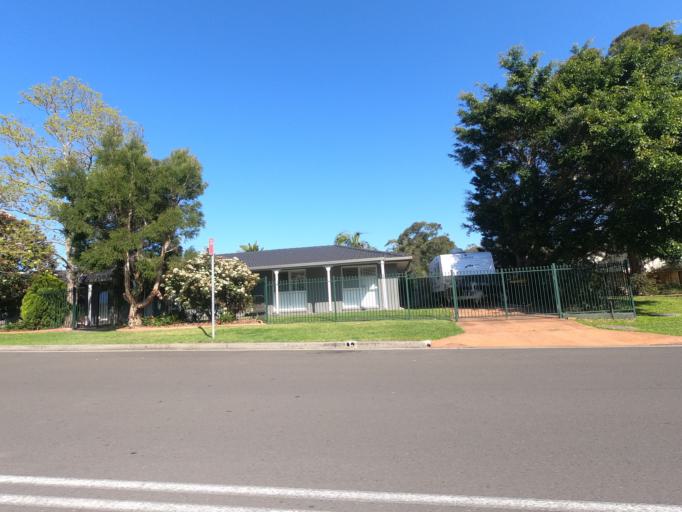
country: AU
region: New South Wales
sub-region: Wollongong
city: Dapto
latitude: -34.4907
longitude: 150.7781
